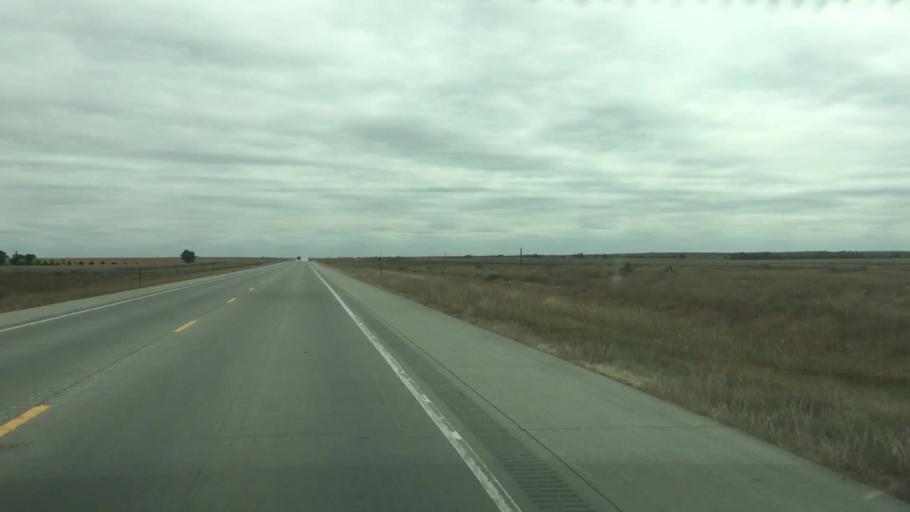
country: US
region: Colorado
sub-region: Kiowa County
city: Eads
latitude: 38.7787
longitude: -102.8939
